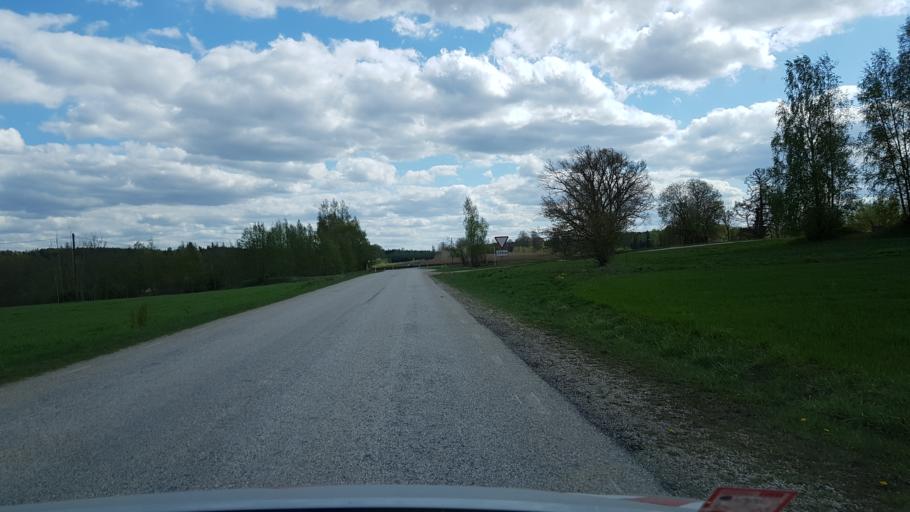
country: EE
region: Tartu
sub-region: UElenurme vald
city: Ulenurme
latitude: 58.2706
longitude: 26.9084
